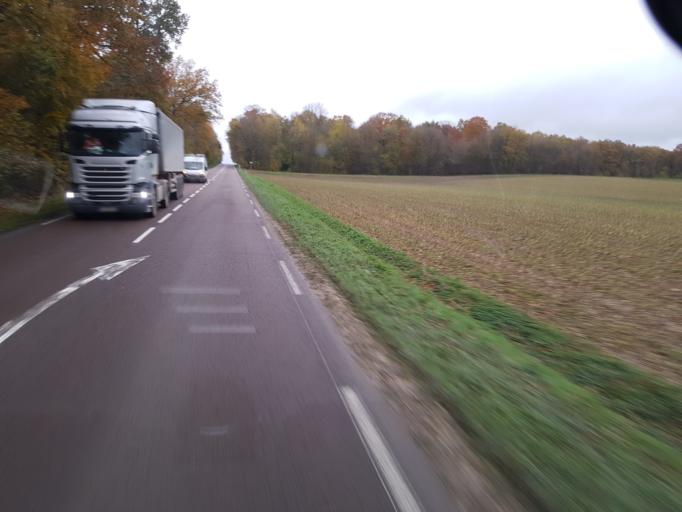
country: FR
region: Champagne-Ardenne
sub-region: Departement de la Marne
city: Esternay
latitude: 48.7951
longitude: 3.6235
